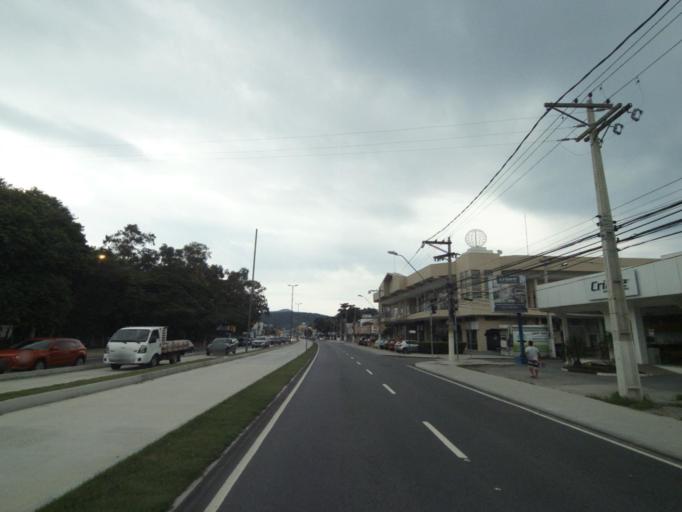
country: BR
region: Rio de Janeiro
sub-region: Niteroi
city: Niteroi
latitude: -22.9343
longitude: -43.0652
